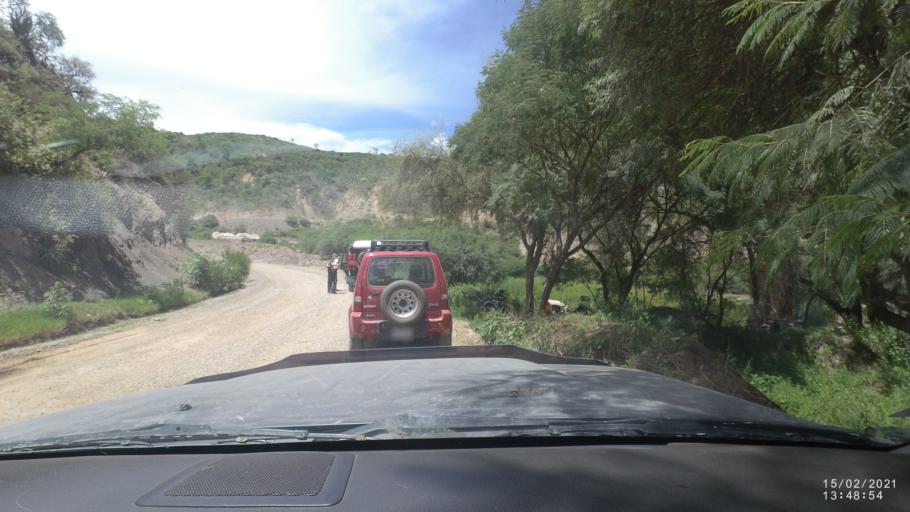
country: BO
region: Cochabamba
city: Sipe Sipe
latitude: -17.5658
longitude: -66.3552
